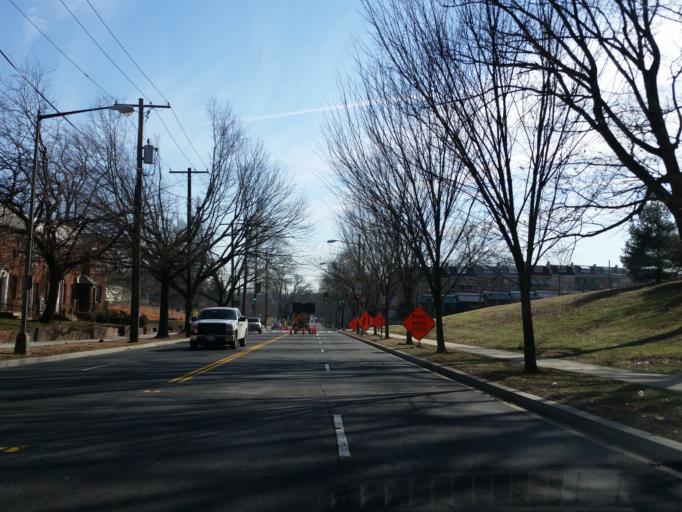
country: US
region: Maryland
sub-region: Montgomery County
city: Takoma Park
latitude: 38.9606
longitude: -77.0271
